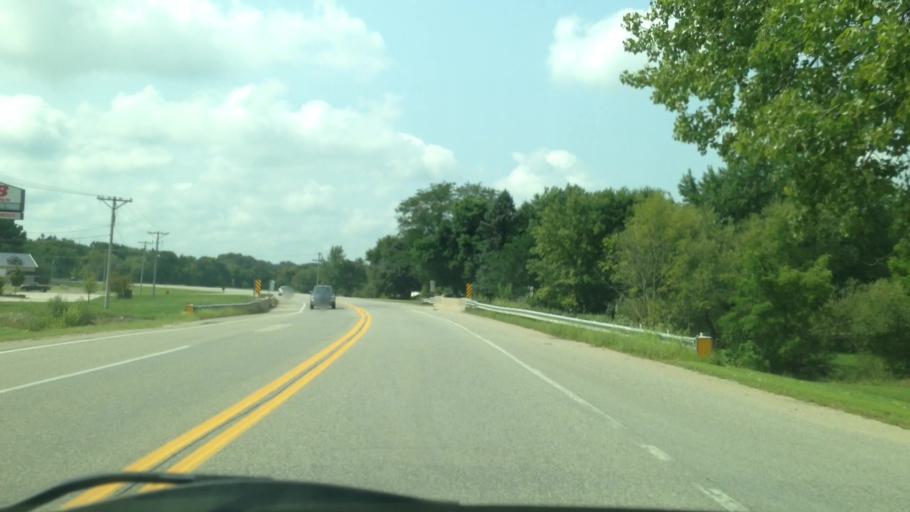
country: US
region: Iowa
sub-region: Linn County
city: Fairfax
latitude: 41.9273
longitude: -91.7824
